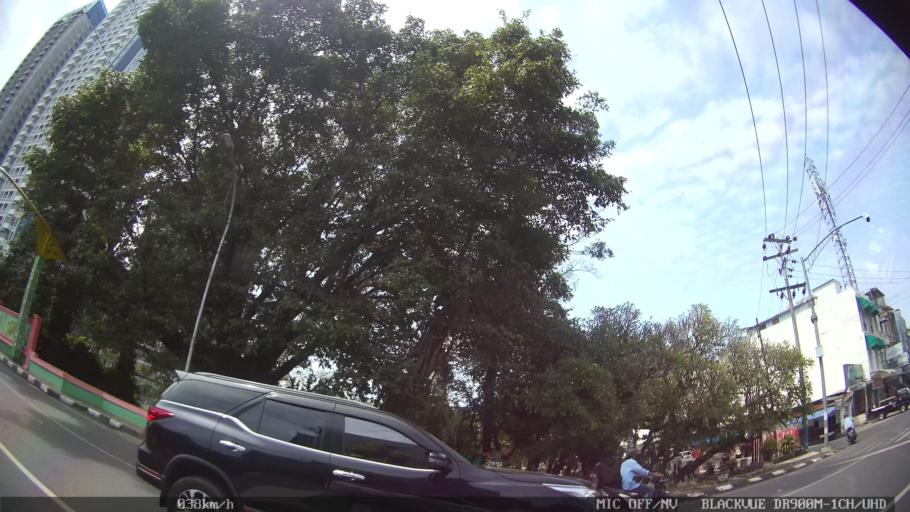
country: ID
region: North Sumatra
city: Medan
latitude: 3.5944
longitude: 98.6729
